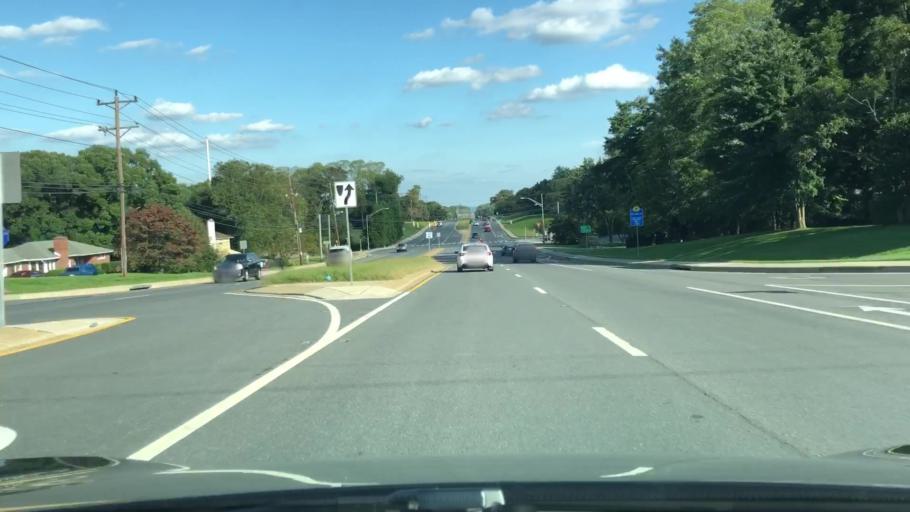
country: US
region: Delaware
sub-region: New Castle County
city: Claymont
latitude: 39.8264
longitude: -75.5114
